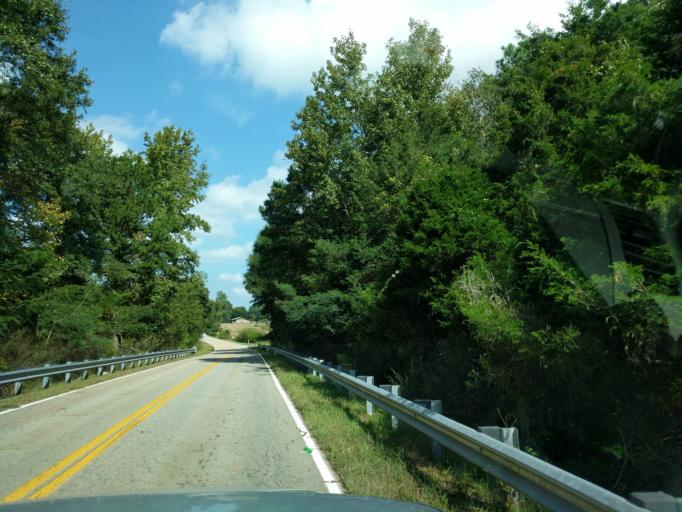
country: US
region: Georgia
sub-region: Hart County
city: Reed Creek
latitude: 34.5149
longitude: -82.8814
